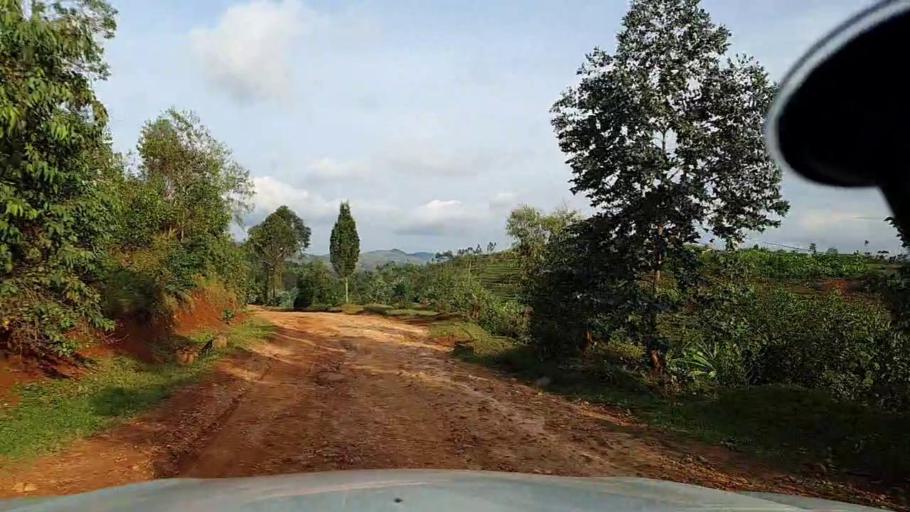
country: RW
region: Southern Province
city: Gitarama
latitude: -2.1862
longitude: 29.5660
